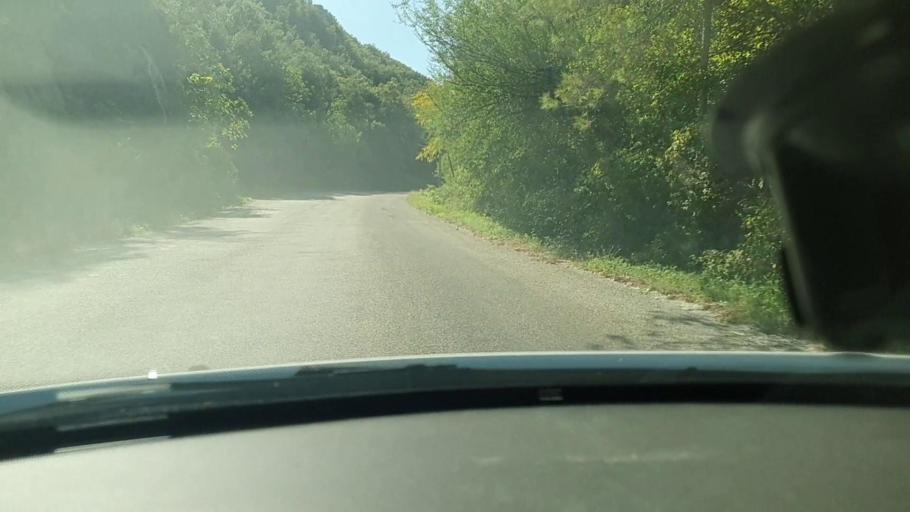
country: FR
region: Languedoc-Roussillon
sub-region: Departement du Gard
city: Goudargues
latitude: 44.1670
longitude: 4.4420
